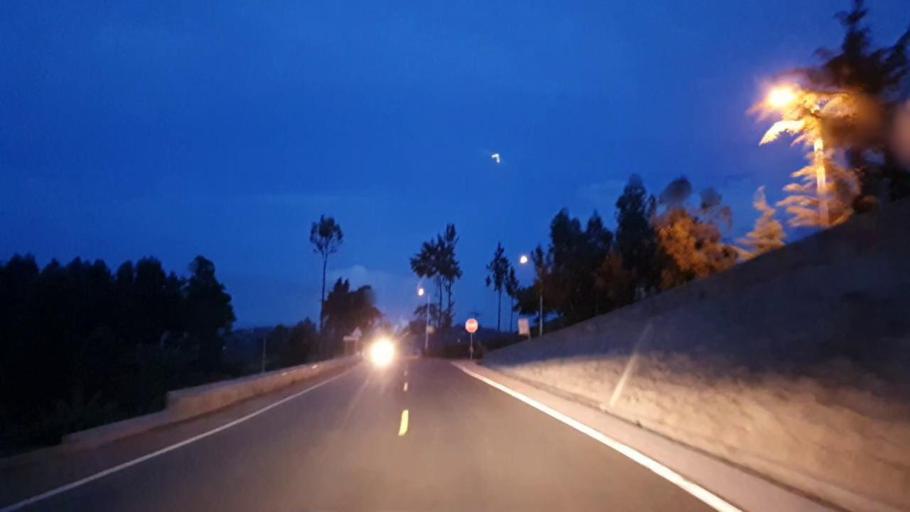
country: RW
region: Southern Province
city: Gikongoro
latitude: -2.4654
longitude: 29.5740
